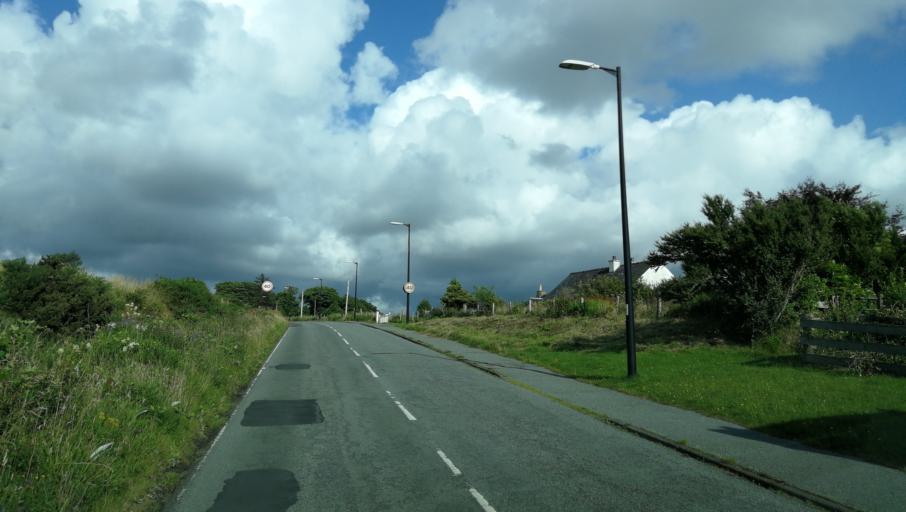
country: GB
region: Scotland
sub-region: Highland
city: Isle of Skye
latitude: 57.4365
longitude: -6.5779
